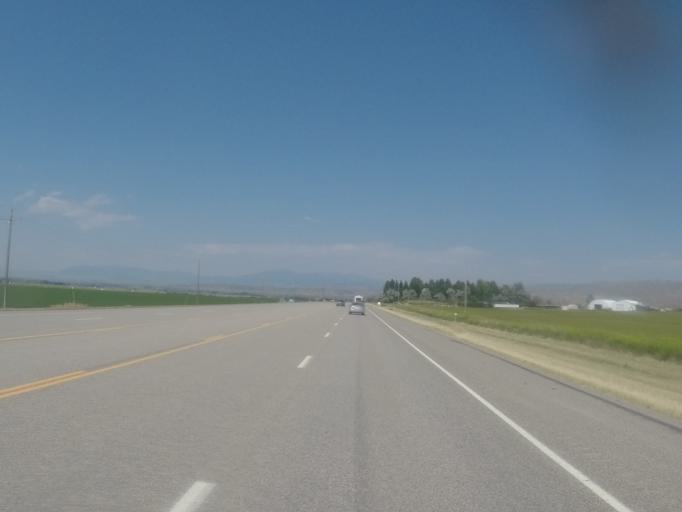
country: US
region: Montana
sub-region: Broadwater County
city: Townsend
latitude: 46.1382
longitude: -111.4796
